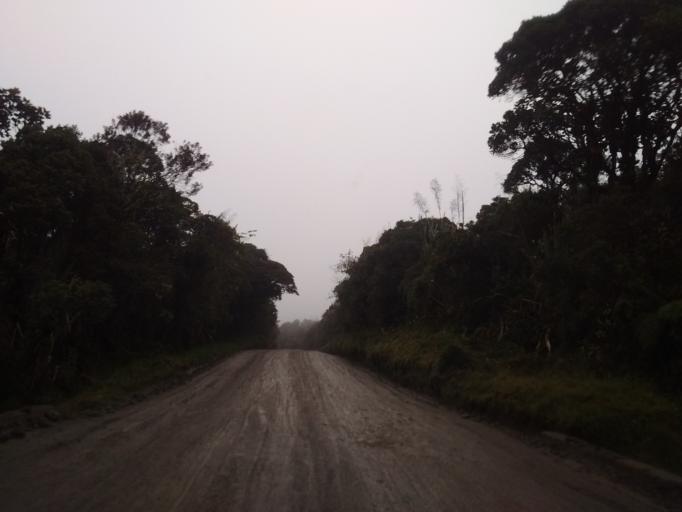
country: CO
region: Cauca
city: Paispamba
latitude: 2.1482
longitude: -76.4413
